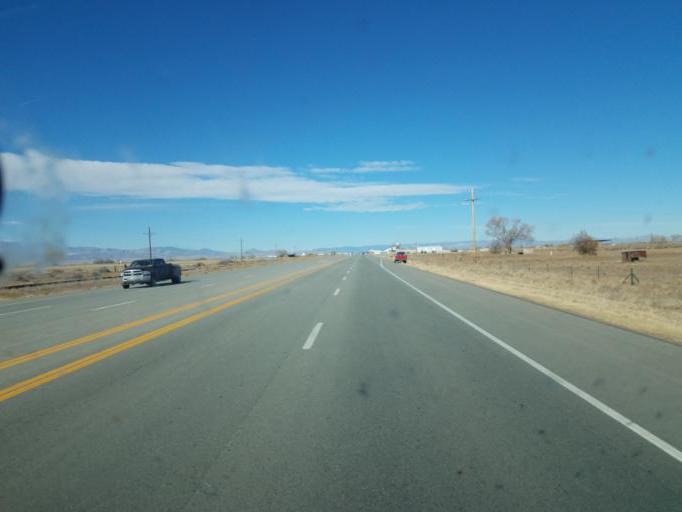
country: US
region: Colorado
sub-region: Rio Grande County
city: Monte Vista
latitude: 37.5273
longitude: -106.0175
